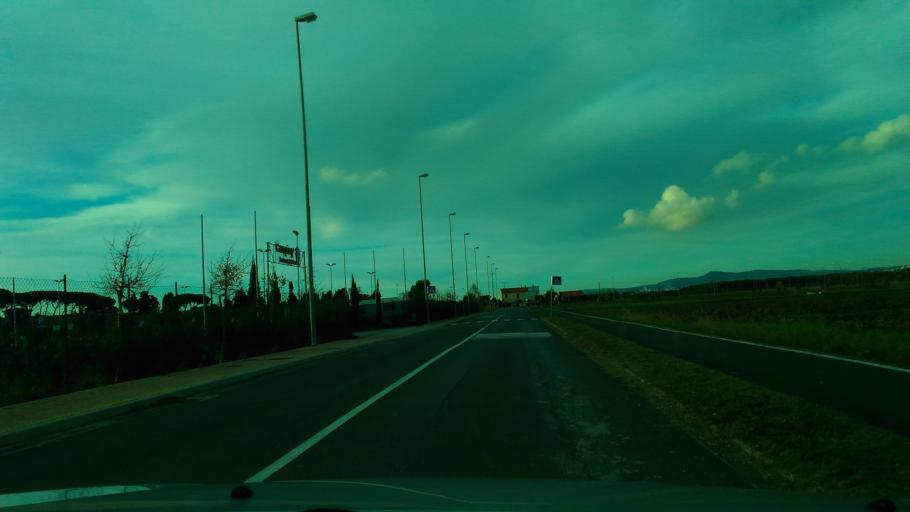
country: IT
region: Tuscany
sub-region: Provincia di Livorno
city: S.P. in Palazzi
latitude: 43.3090
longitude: 10.4888
